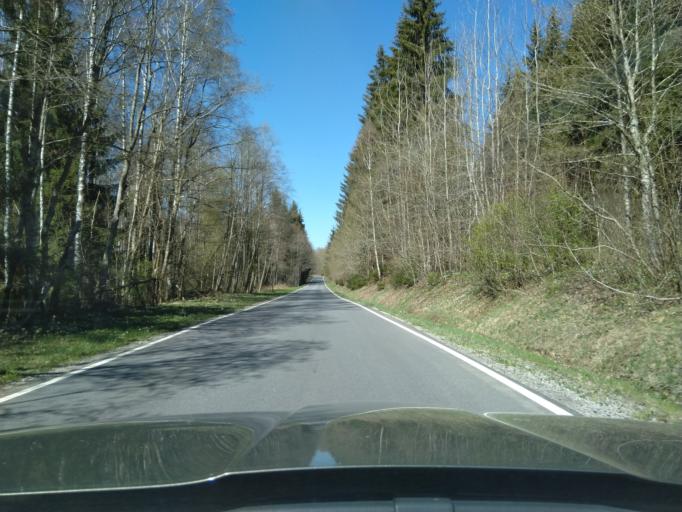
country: CZ
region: Jihocesky
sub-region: Okres Prachatice
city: Vimperk
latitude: 48.9504
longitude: 13.7841
